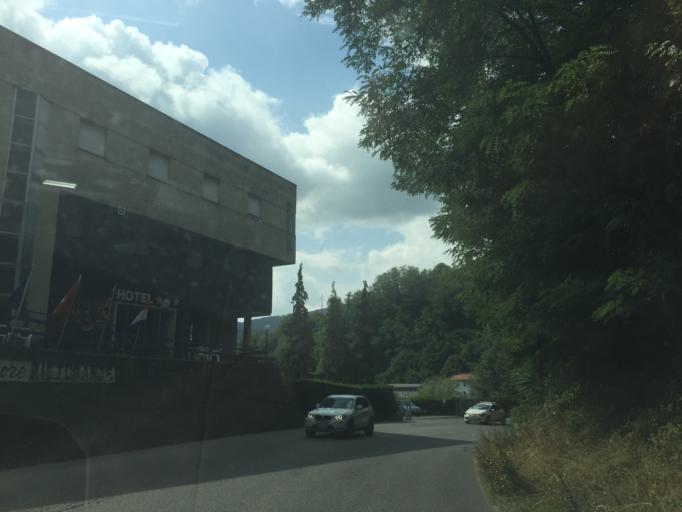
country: IT
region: Tuscany
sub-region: Provincia di Pistoia
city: San Marcello Pistoiese
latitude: 44.0566
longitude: 10.7826
